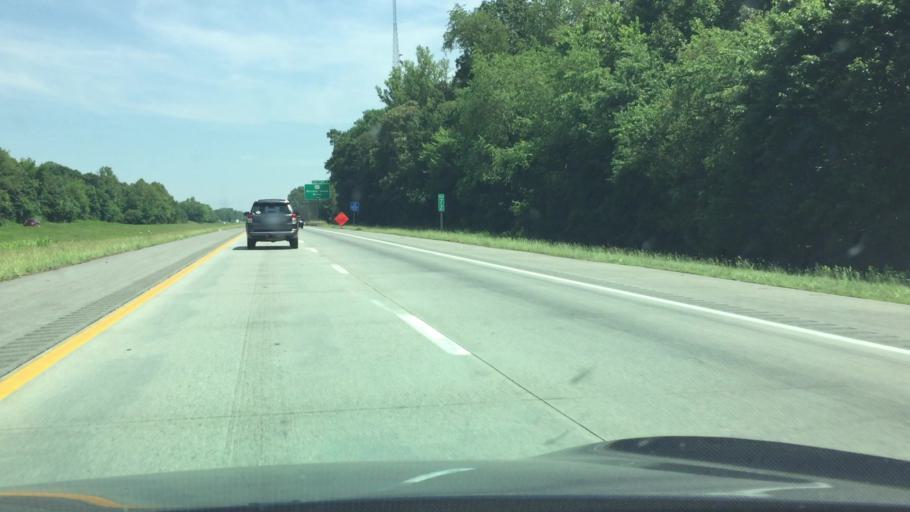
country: US
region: North Carolina
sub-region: Yadkin County
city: Jonesville
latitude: 36.0999
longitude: -80.8124
